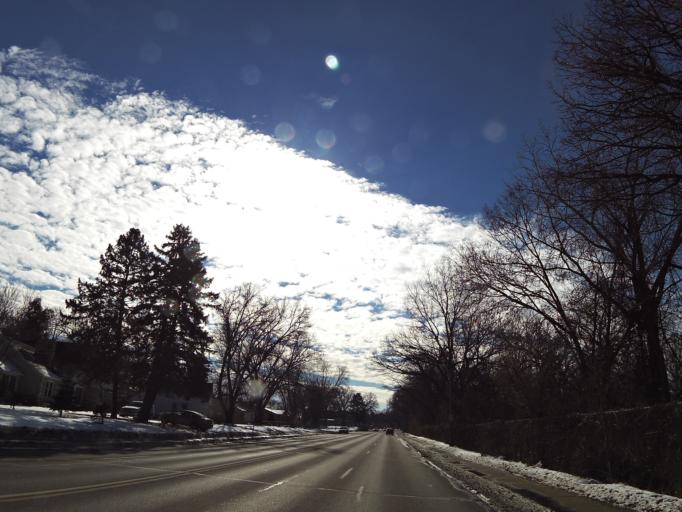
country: US
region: Minnesota
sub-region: Hennepin County
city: Richfield
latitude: 44.8797
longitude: -93.2880
